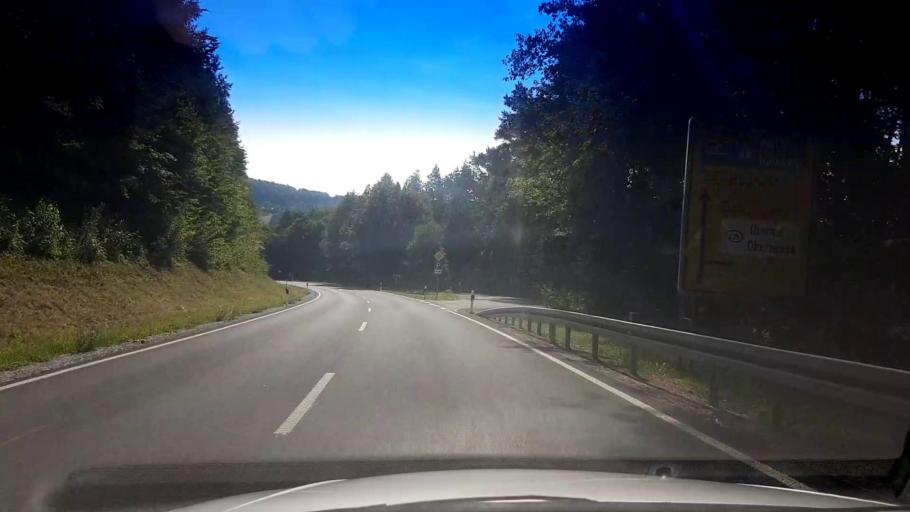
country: DE
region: Bavaria
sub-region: Upper Franconia
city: Plankenfels
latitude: 49.9336
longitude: 11.3830
